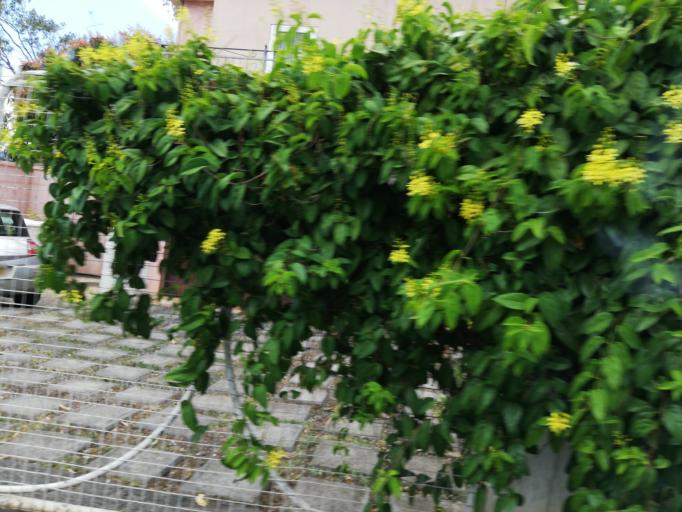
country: MU
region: Moka
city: Pailles
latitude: -20.2060
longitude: 57.4725
